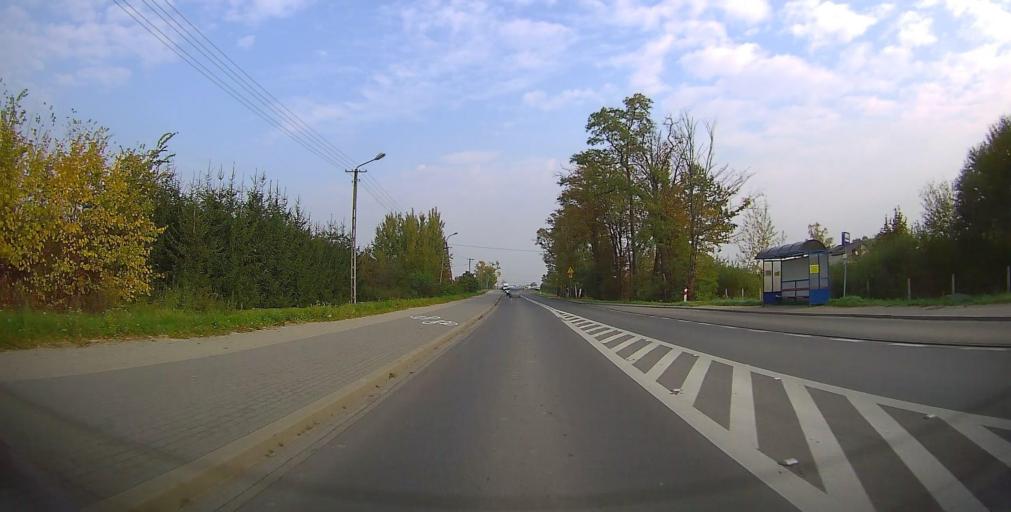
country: PL
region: Masovian Voivodeship
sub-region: Powiat grojecki
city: Mogielnica
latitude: 51.7071
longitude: 20.7386
